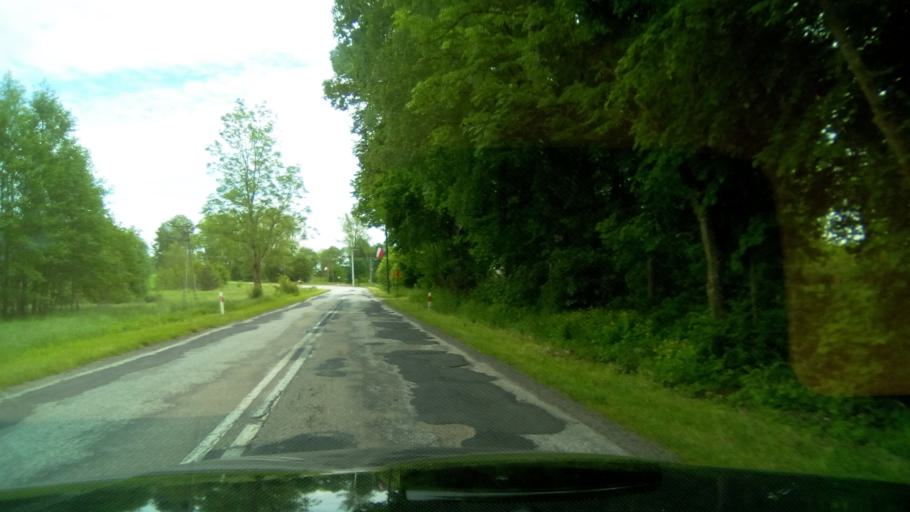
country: PL
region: Pomeranian Voivodeship
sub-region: Powiat bytowski
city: Czarna Dabrowka
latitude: 54.3182
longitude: 17.4961
